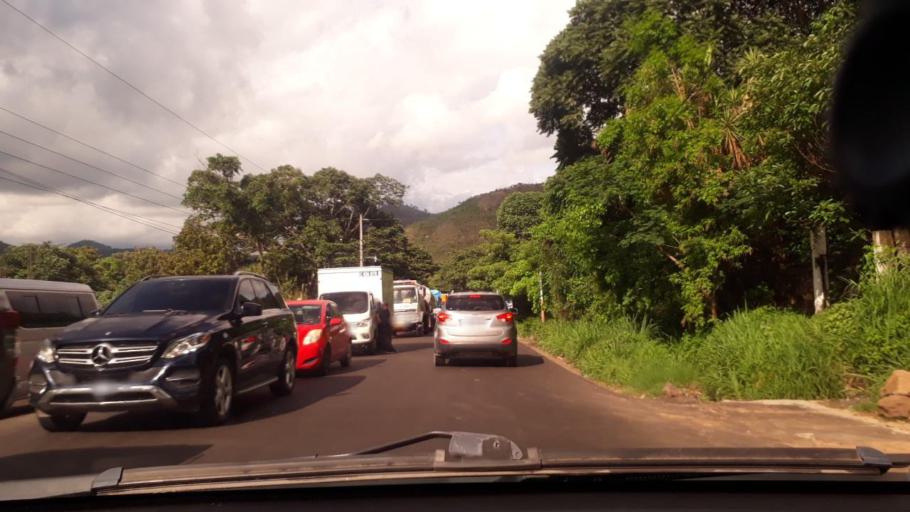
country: GT
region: Jutiapa
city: Quesada
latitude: 14.2709
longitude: -90.0069
